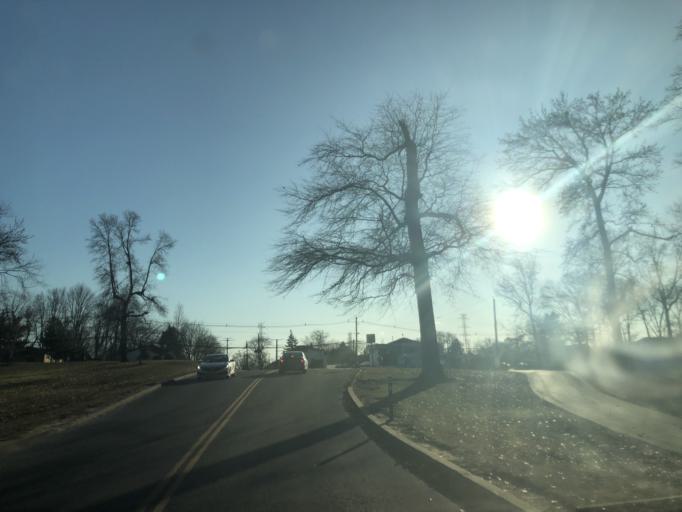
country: US
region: New Jersey
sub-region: Middlesex County
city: Metuchen
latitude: 40.5411
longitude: -74.3416
